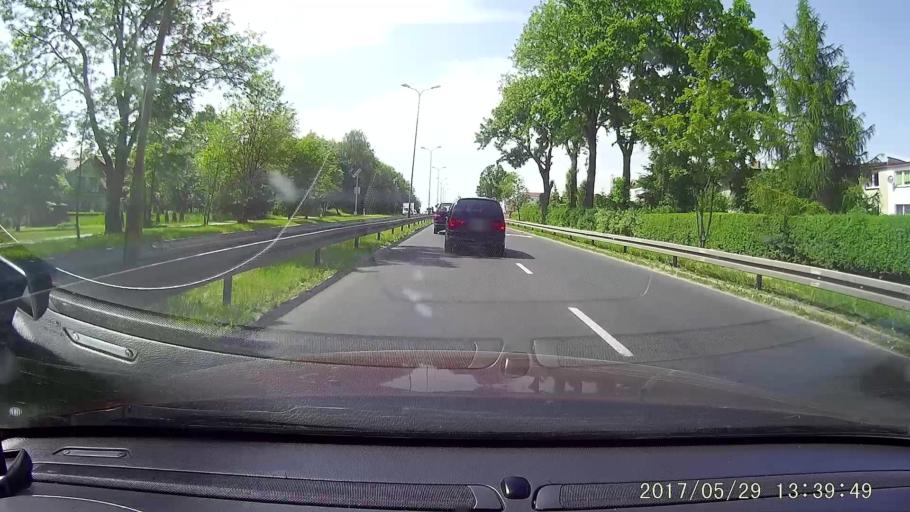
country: PL
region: Lower Silesian Voivodeship
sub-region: Powiat lubanski
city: Luban
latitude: 51.1296
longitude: 15.2824
